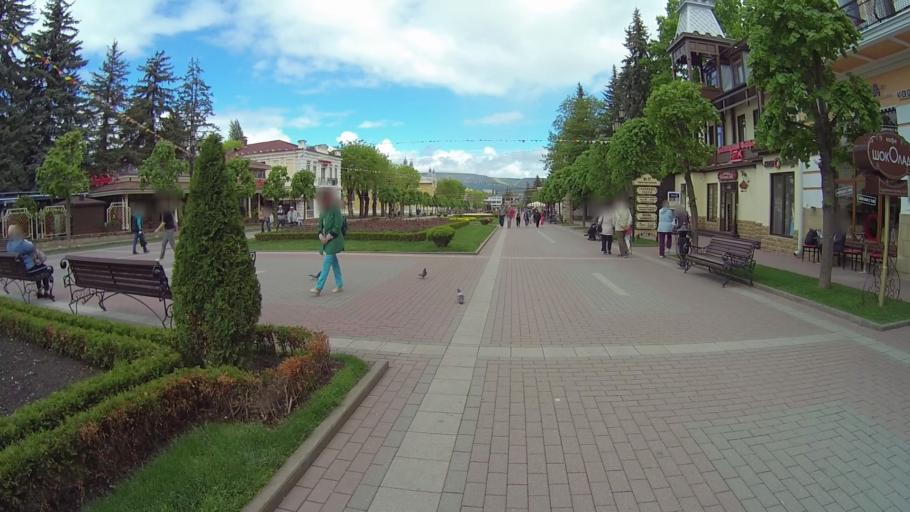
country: RU
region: Stavropol'skiy
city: Kislovodsk
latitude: 43.9011
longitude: 42.7170
